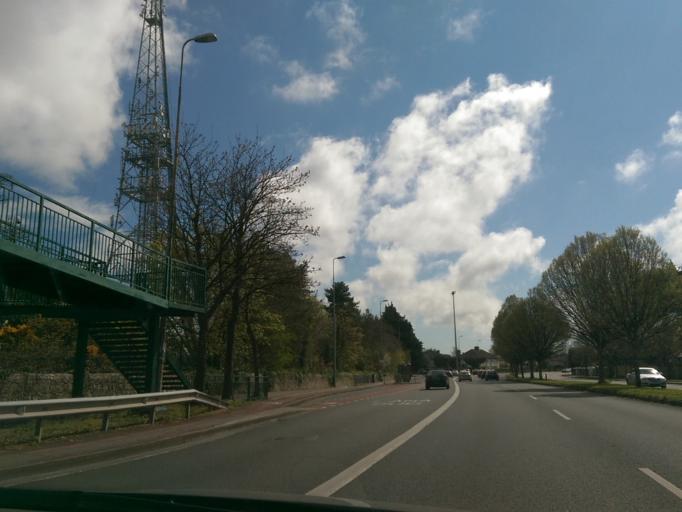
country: IE
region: Leinster
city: Donnybrook
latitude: 53.3149
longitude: -6.2257
